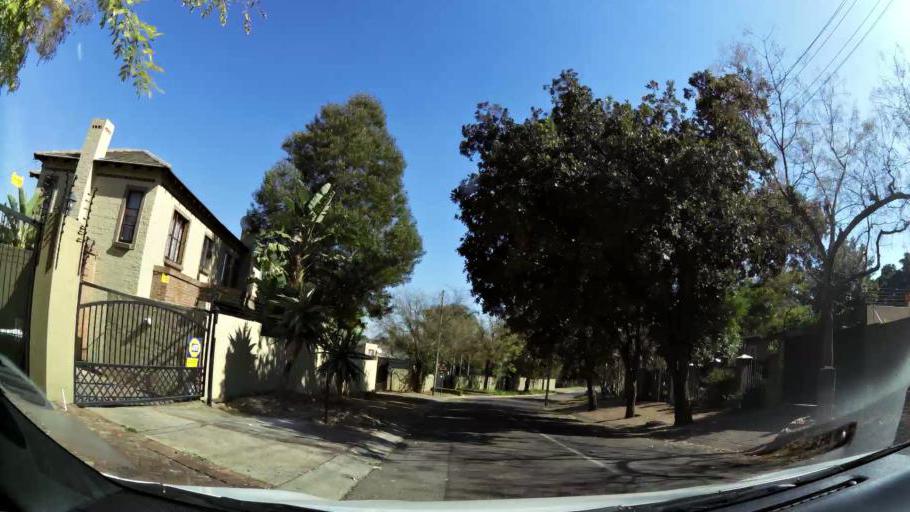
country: ZA
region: Gauteng
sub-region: City of Tshwane Metropolitan Municipality
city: Pretoria
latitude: -25.7963
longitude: 28.2291
